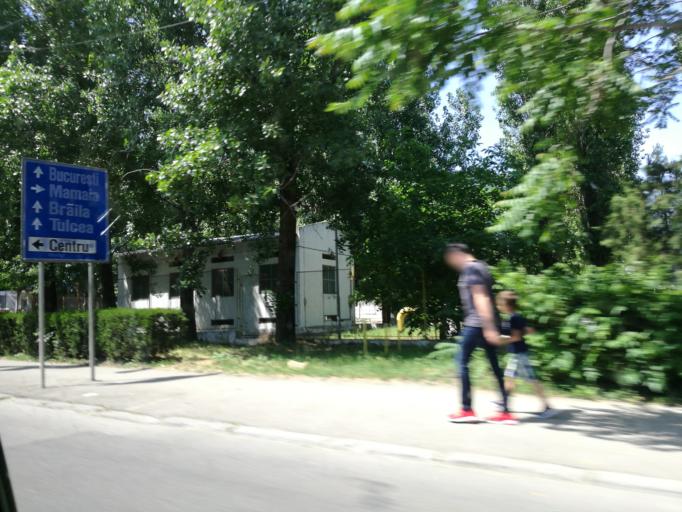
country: RO
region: Constanta
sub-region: Municipiul Constanta
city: Constanta
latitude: 44.2027
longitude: 28.6337
